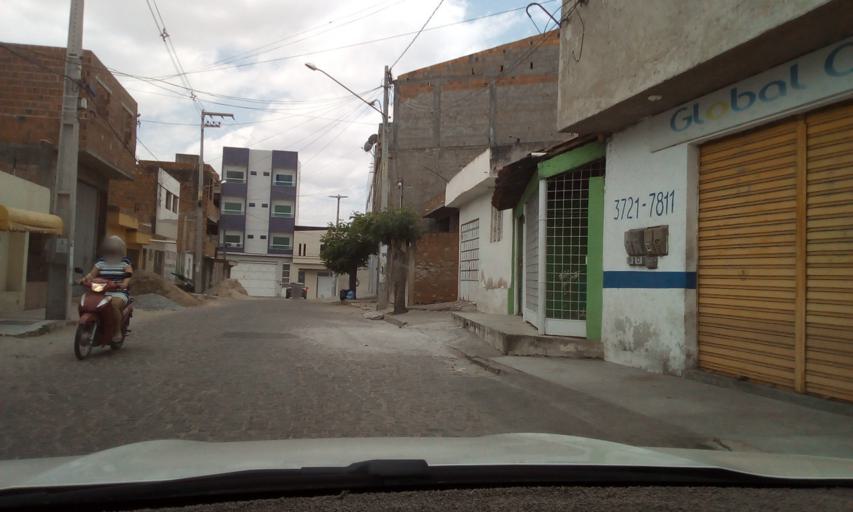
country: BR
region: Pernambuco
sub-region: Caruaru
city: Caruaru
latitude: -8.2749
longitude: -35.9831
